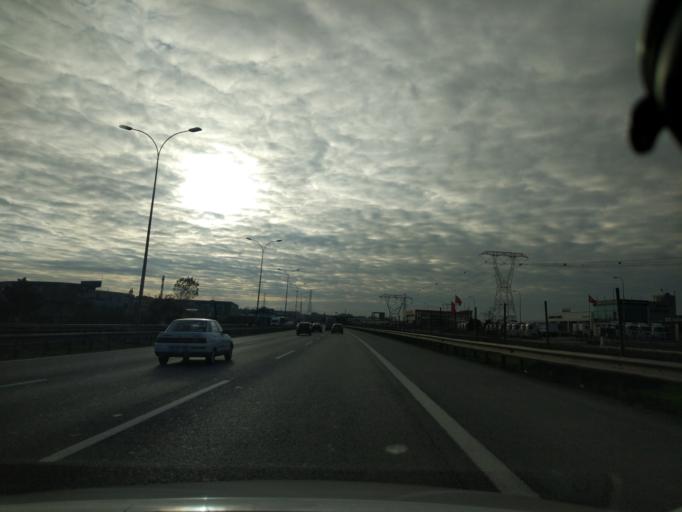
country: TR
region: Istanbul
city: Icmeler
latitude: 40.9109
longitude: 29.3571
